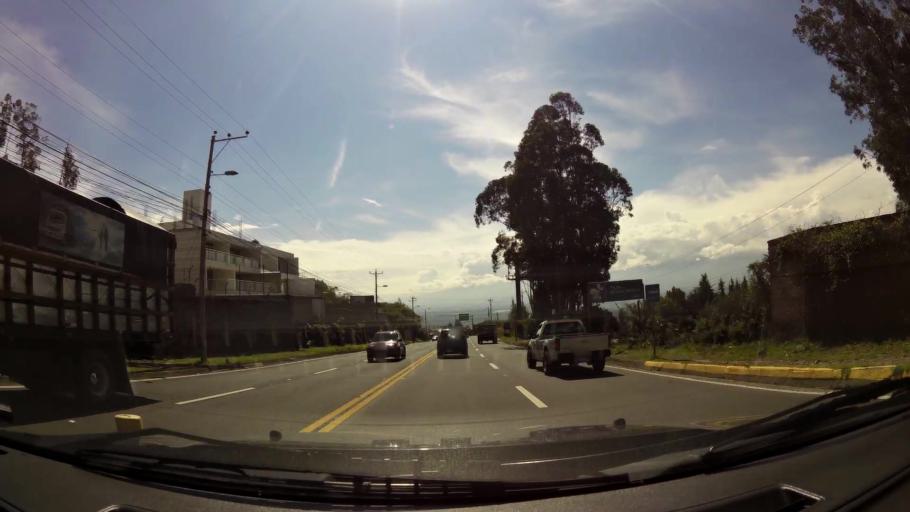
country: EC
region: Pichincha
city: Quito
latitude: -0.1917
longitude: -78.4508
